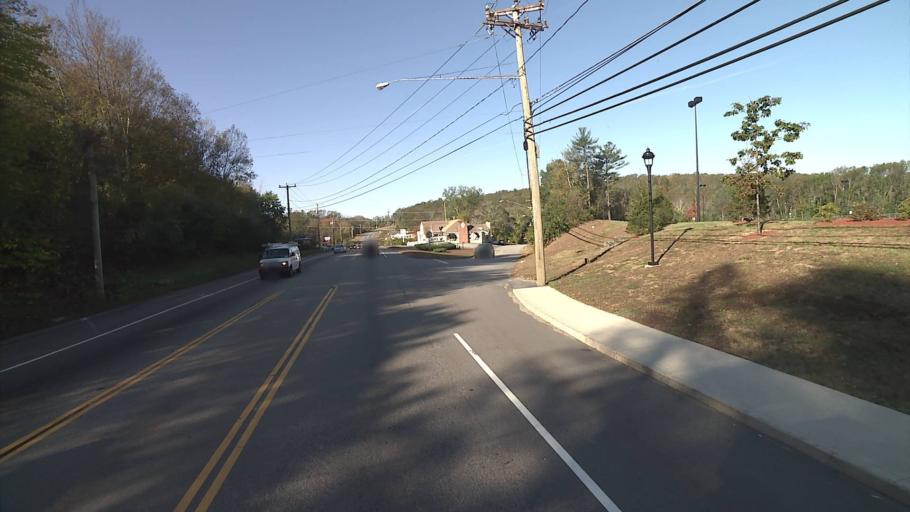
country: US
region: Connecticut
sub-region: Windham County
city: East Brooklyn
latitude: 41.7970
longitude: -71.9134
